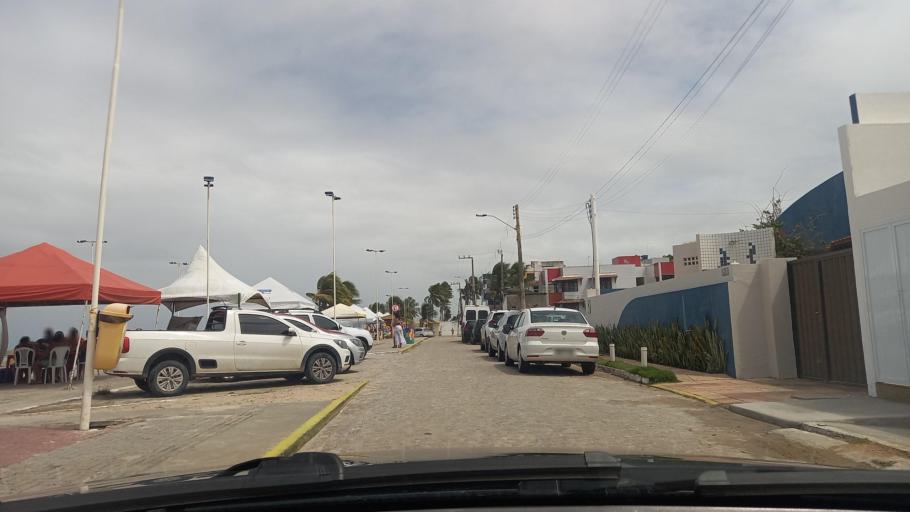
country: BR
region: Alagoas
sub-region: Marechal Deodoro
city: Marechal Deodoro
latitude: -9.8379
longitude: -35.8883
